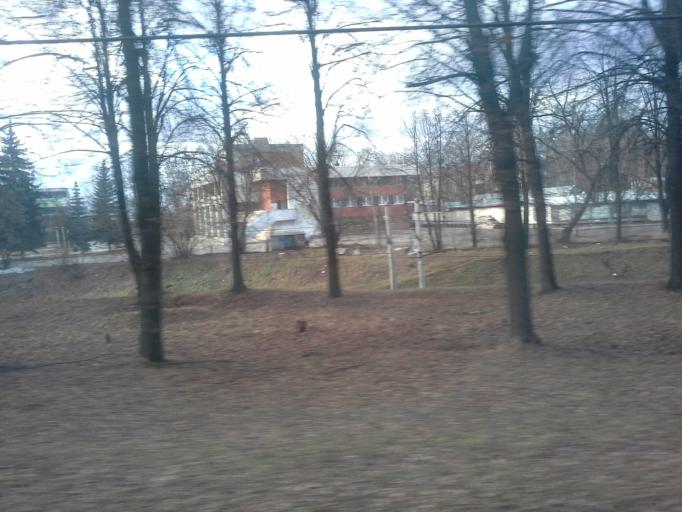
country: RU
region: Moskovskaya
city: Mytishchi
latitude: 55.9273
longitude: 37.7762
